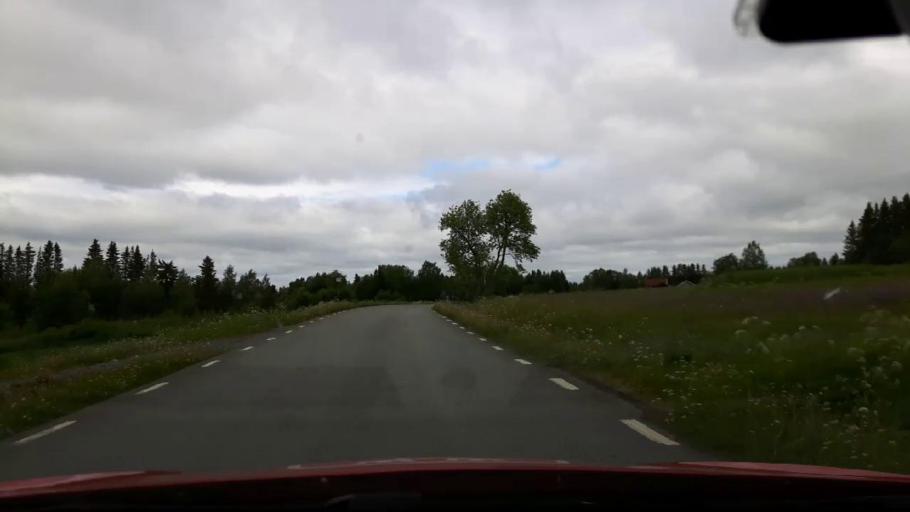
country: SE
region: Jaemtland
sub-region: Krokoms Kommun
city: Krokom
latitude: 63.2623
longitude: 14.5373
